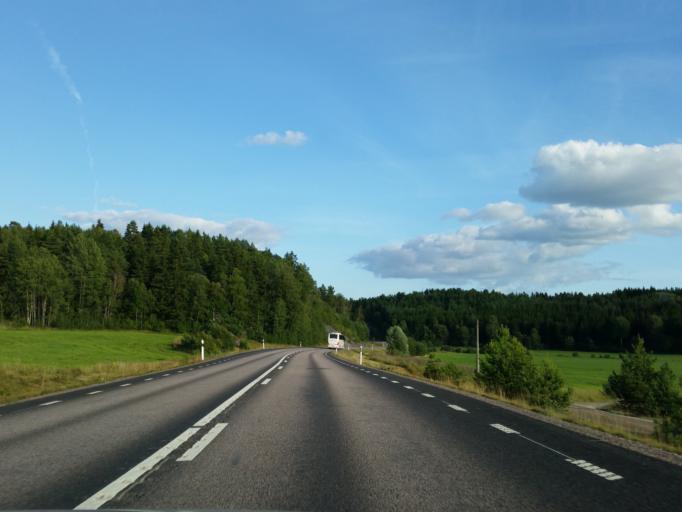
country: SE
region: Soedermanland
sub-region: Gnesta Kommun
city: Gnesta
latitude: 59.0394
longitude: 17.2961
